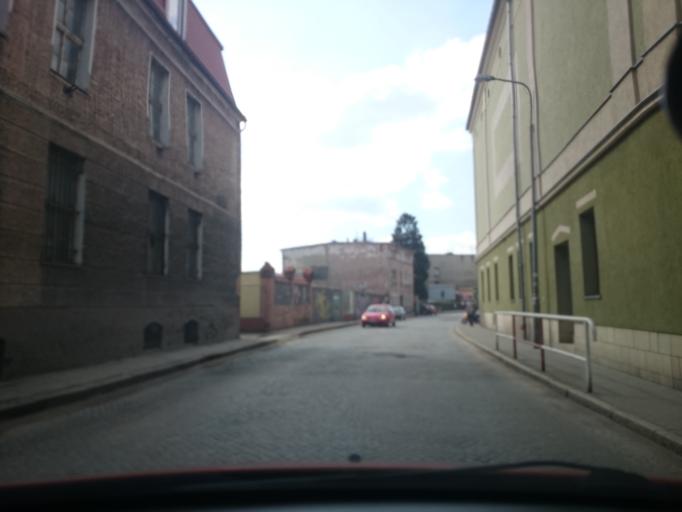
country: PL
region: Lower Silesian Voivodeship
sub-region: Powiat klodzki
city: Bystrzyca Klodzka
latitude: 50.2981
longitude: 16.6495
